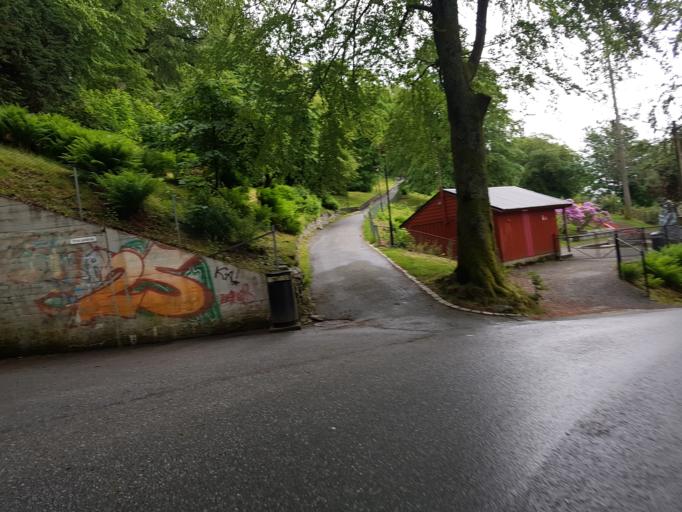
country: NO
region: Hordaland
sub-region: Bergen
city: Bergen
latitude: 60.3978
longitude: 5.3311
